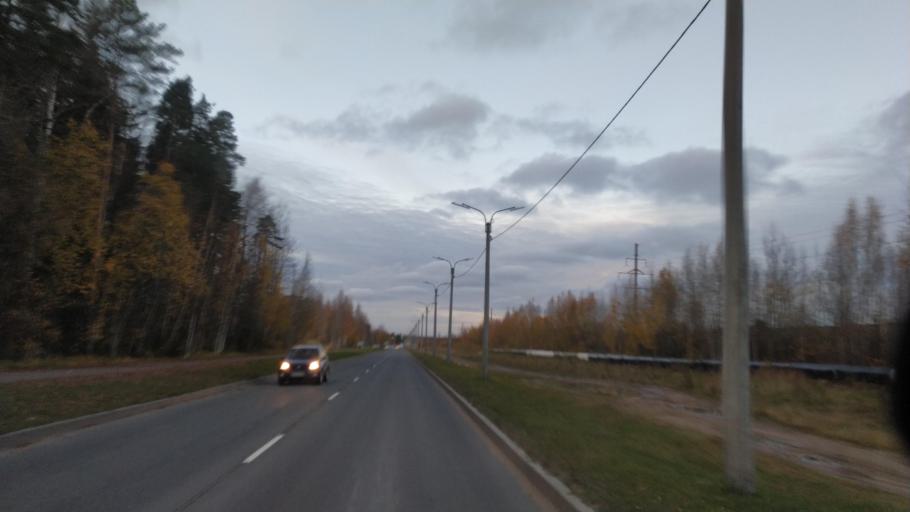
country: RU
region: Leningrad
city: Sosnovyy Bor
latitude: 59.9090
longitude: 29.1012
